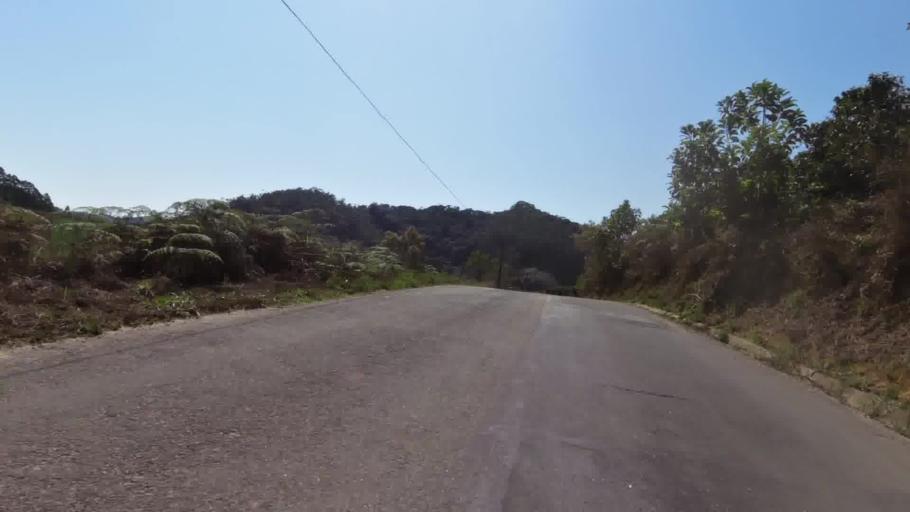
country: BR
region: Espirito Santo
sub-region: Marechal Floriano
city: Marechal Floriano
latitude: -20.4296
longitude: -40.8756
